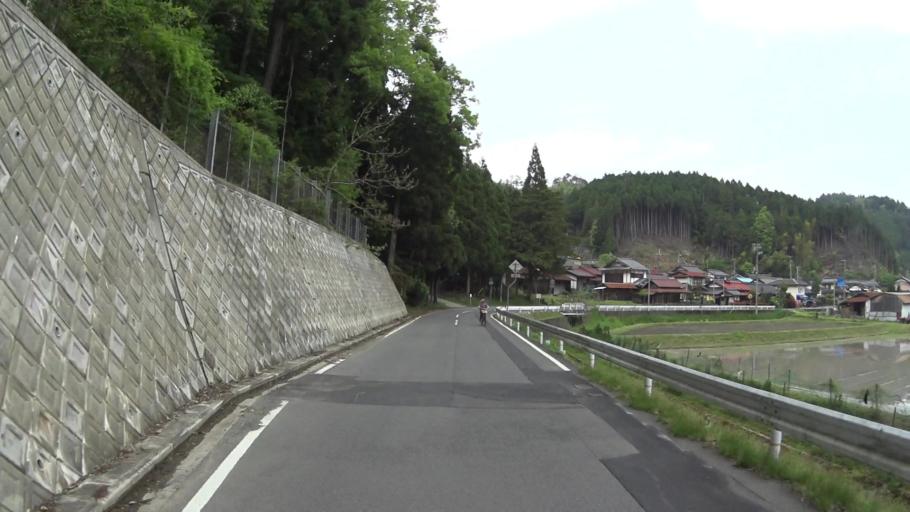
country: JP
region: Kyoto
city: Kameoka
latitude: 35.1247
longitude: 135.6224
